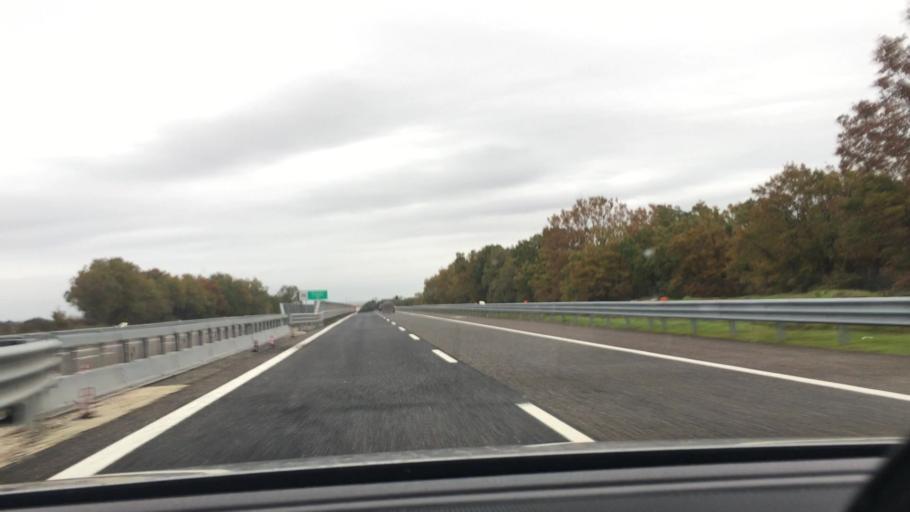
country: IT
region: Apulia
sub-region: Provincia di Bari
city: Gioia del Colle
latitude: 40.7506
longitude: 16.9165
